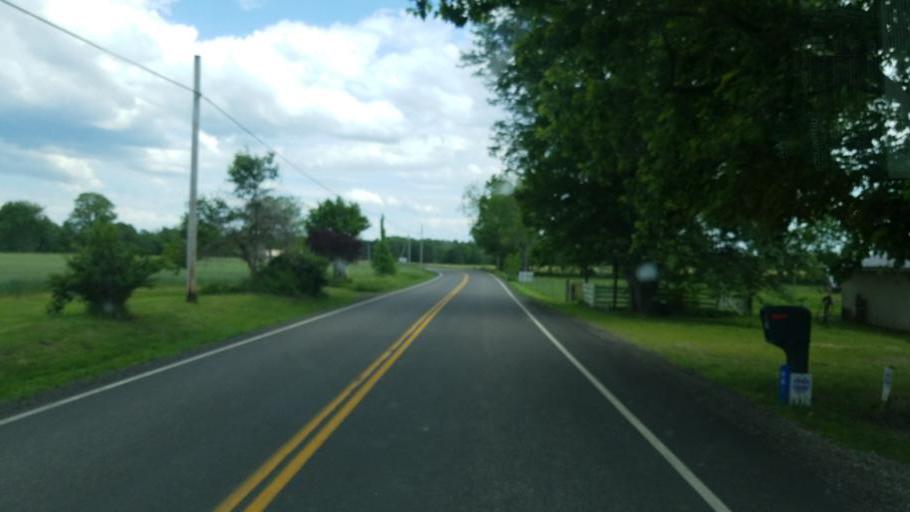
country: US
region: Ohio
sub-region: Huron County
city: Greenwich
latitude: 40.9324
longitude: -82.5393
